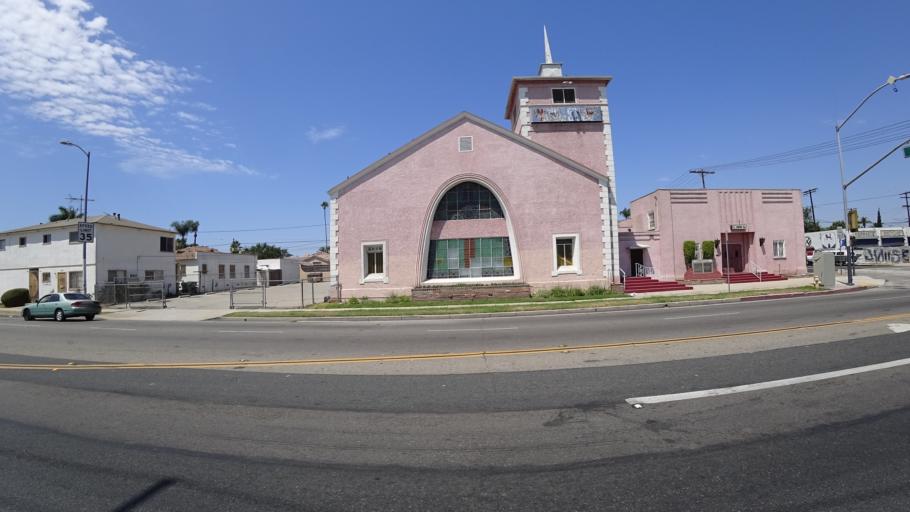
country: US
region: California
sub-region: Los Angeles County
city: Westmont
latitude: 33.9524
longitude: -118.3002
